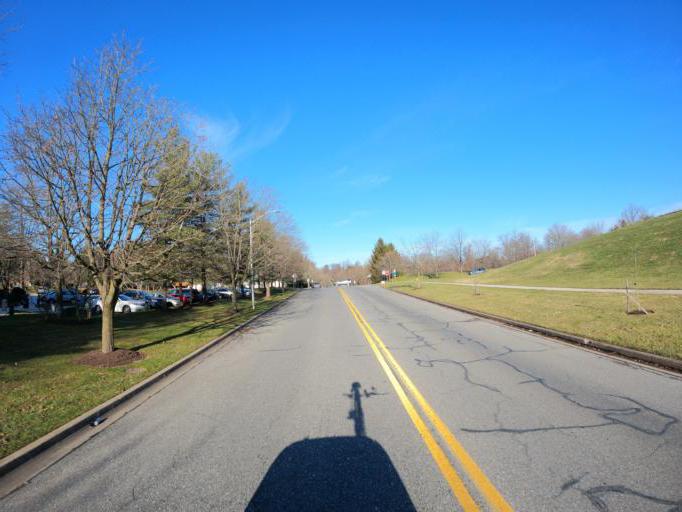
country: US
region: Maryland
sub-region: Montgomery County
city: Olney
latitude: 39.1556
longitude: -77.0580
